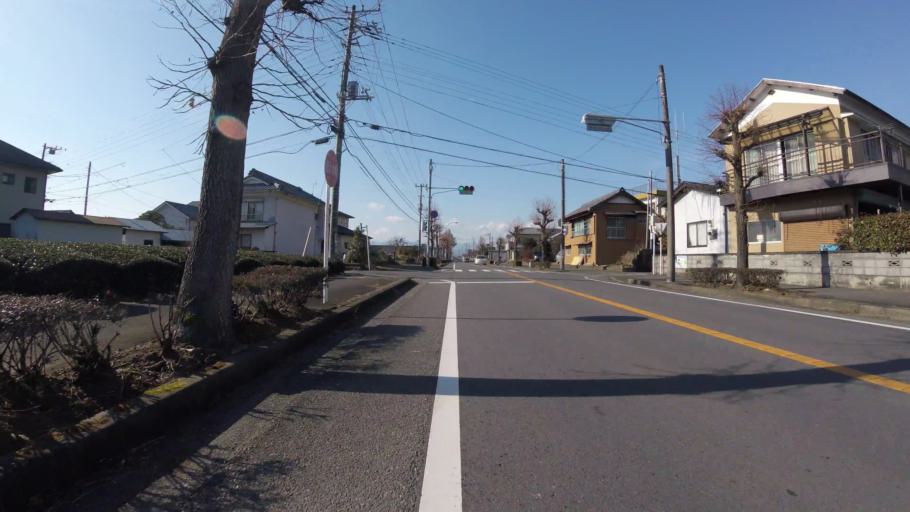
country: JP
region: Shizuoka
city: Fuji
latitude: 35.1509
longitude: 138.7633
